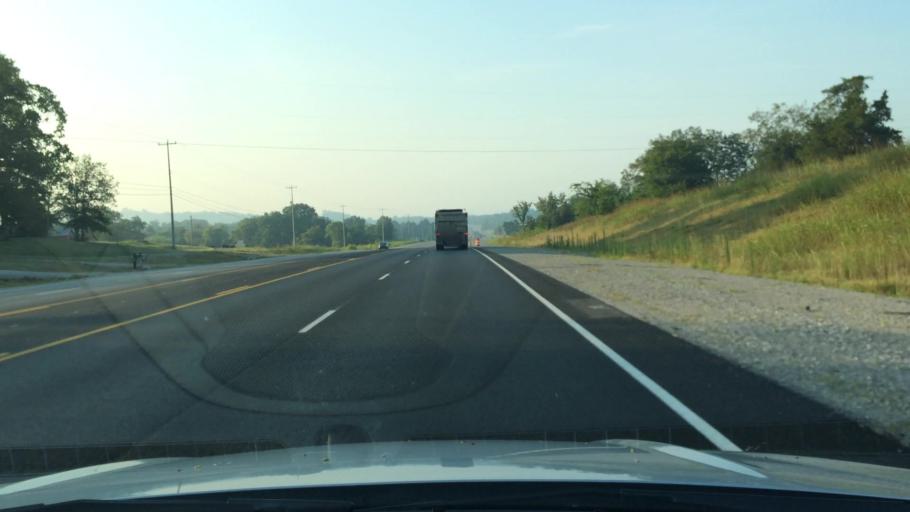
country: US
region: Tennessee
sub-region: Giles County
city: Pulaski
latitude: 35.1635
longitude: -87.0114
